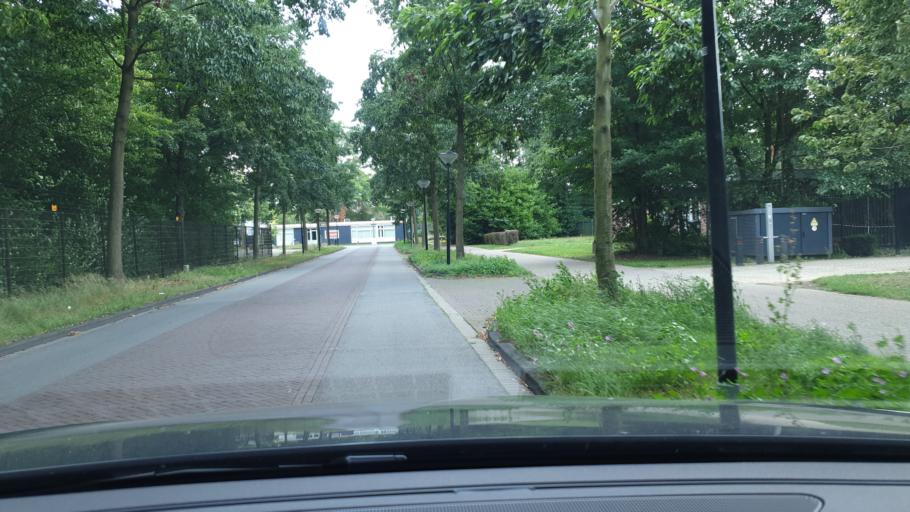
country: NL
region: North Brabant
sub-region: Gemeente Eindhoven
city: Eindhoven
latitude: 51.4143
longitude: 5.4785
